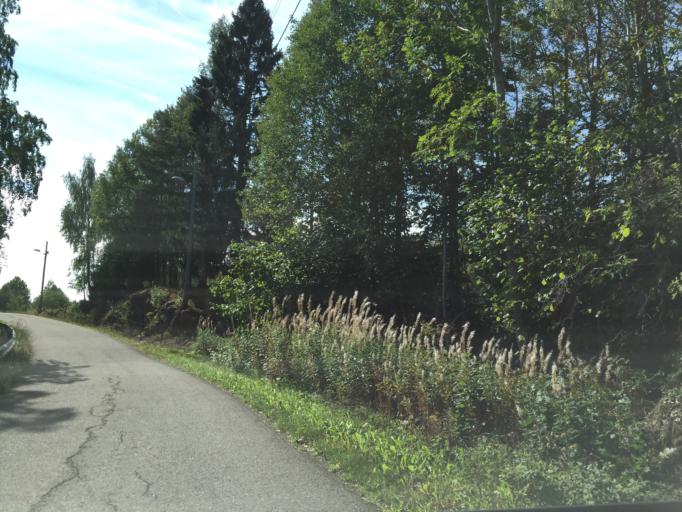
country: NO
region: Vestfold
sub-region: Hof
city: Hof
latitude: 59.4727
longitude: 10.1428
